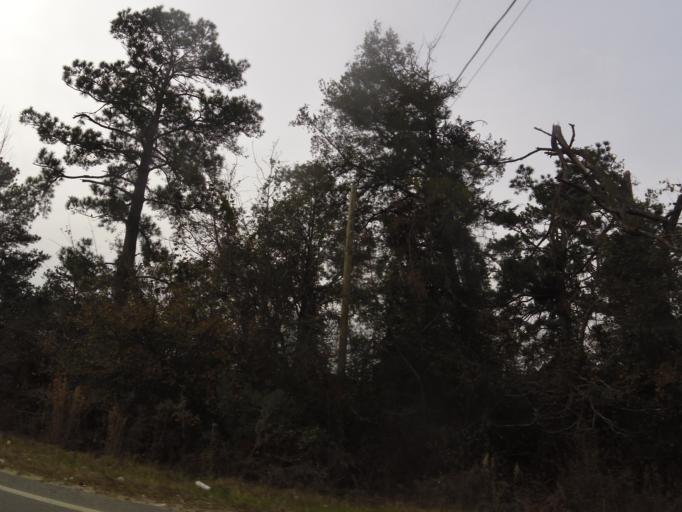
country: US
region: Georgia
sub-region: Decatur County
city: Bainbridge
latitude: 30.9128
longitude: -84.5934
